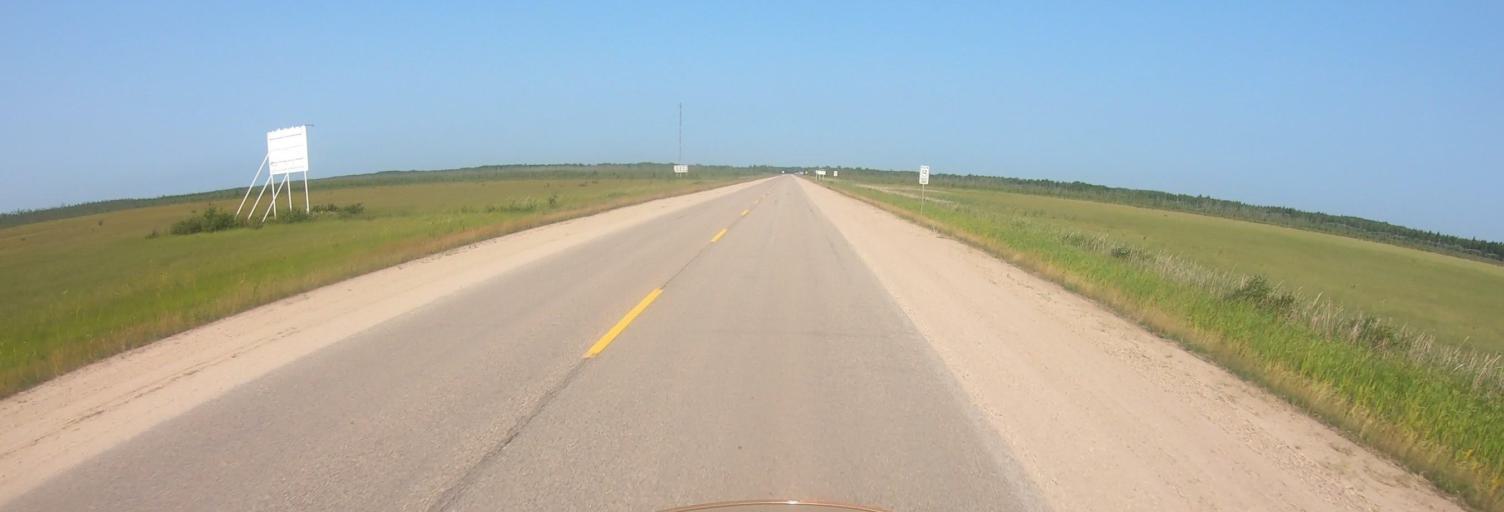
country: US
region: Minnesota
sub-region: Roseau County
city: Warroad
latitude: 49.0088
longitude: -95.3873
